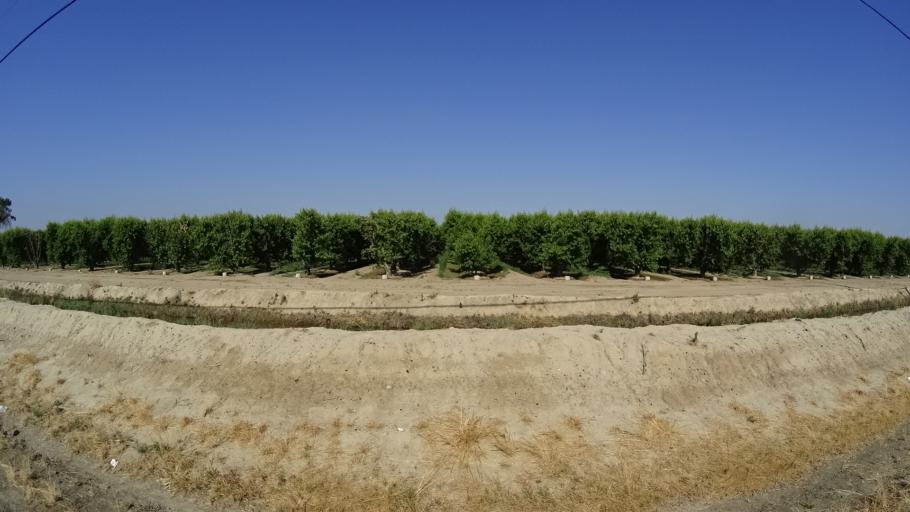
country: US
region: California
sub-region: Fresno County
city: Kingsburg
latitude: 36.4947
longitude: -119.5570
